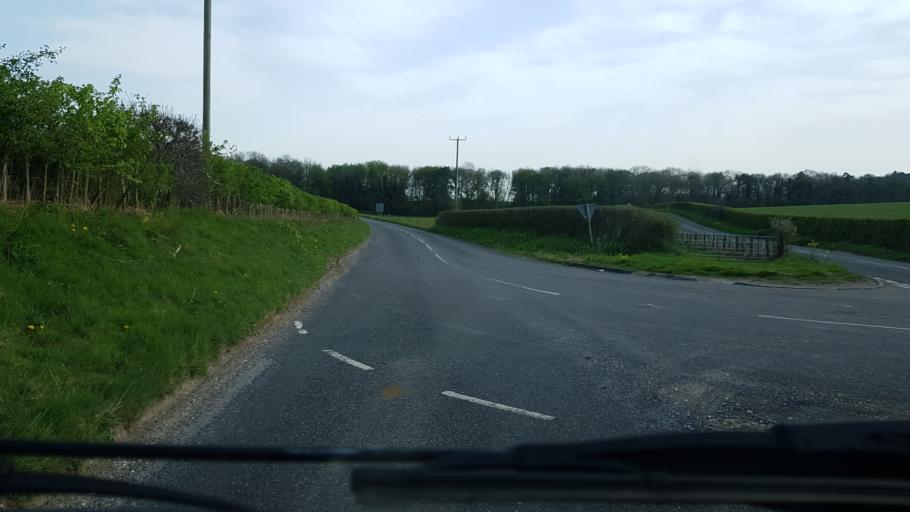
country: GB
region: England
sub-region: Hampshire
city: Kingsclere
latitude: 51.2942
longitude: -1.2667
